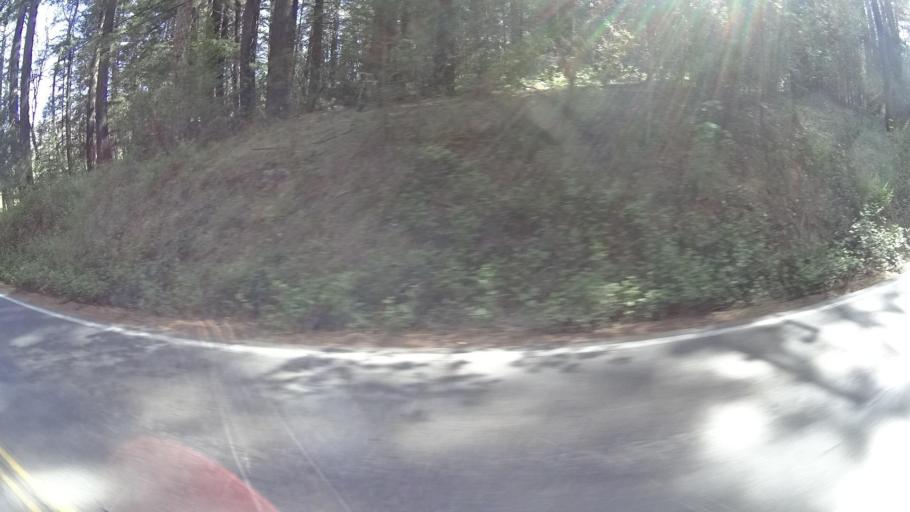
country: US
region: California
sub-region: Lake County
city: Cobb
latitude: 38.8323
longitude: -122.7354
